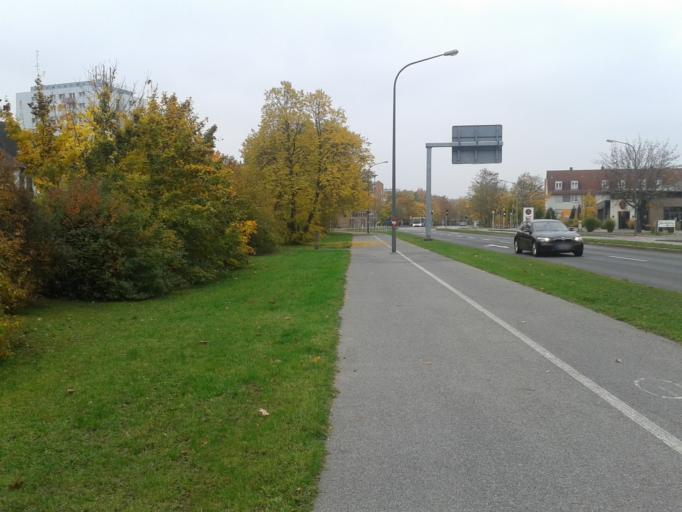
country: DE
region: Bavaria
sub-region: Upper Franconia
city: Bamberg
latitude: 49.9113
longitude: 10.9117
